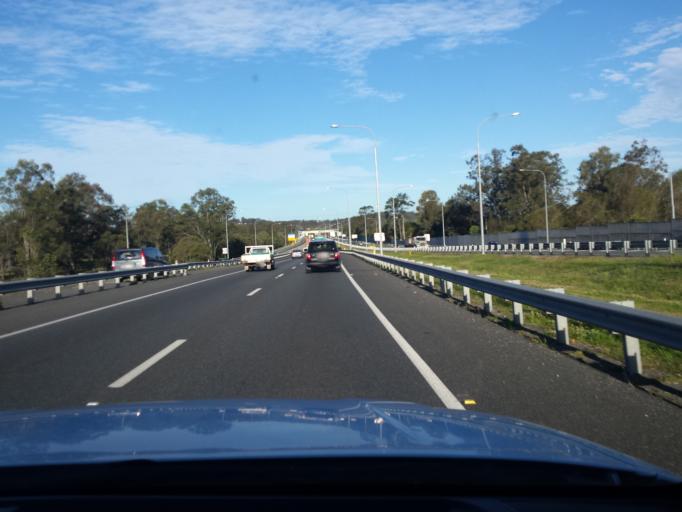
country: AU
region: Queensland
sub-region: Logan
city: Slacks Creek
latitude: -27.6655
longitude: 153.1421
